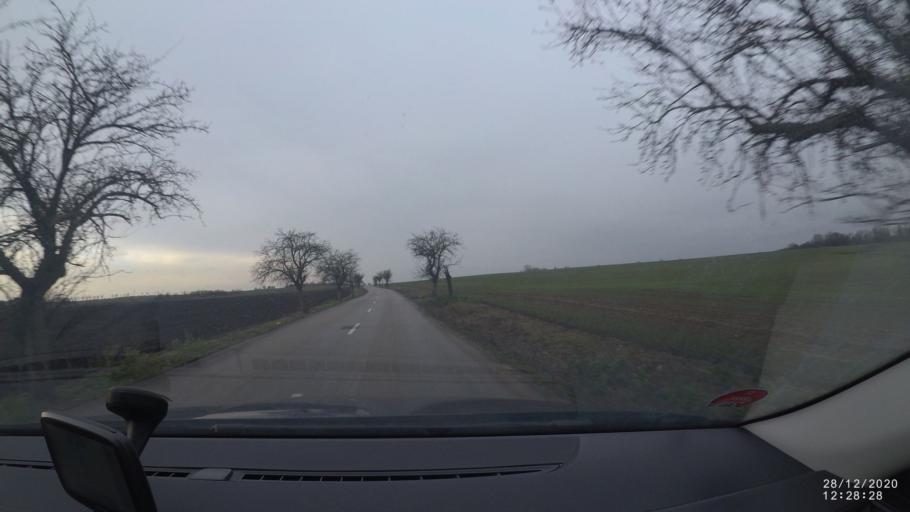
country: CZ
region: Central Bohemia
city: Brandys nad Labem-Stara Boleslav
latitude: 50.1954
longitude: 14.6302
